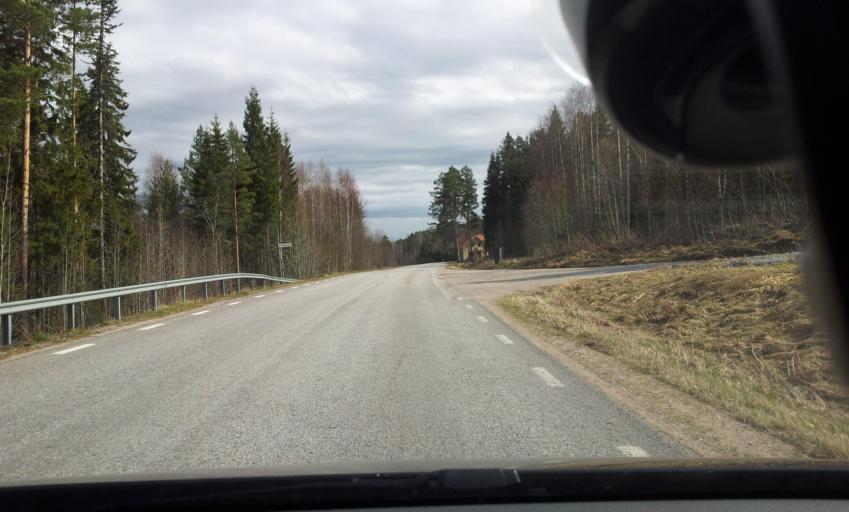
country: SE
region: Gaevleborg
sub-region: Ljusdals Kommun
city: Ljusdal
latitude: 61.7683
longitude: 16.0227
